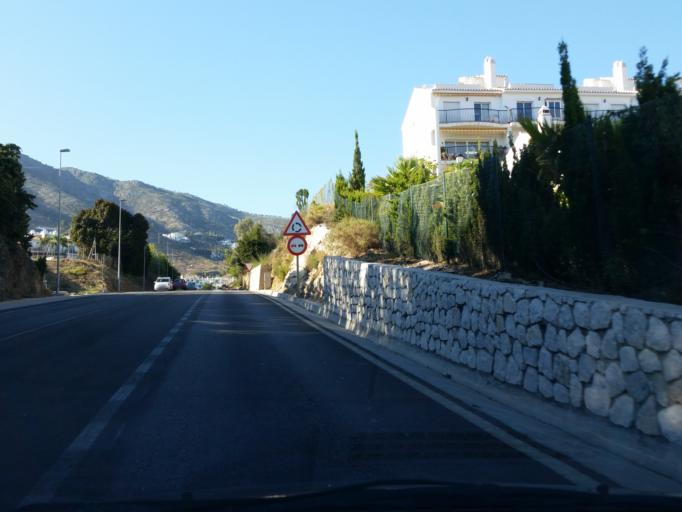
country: ES
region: Andalusia
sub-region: Provincia de Malaga
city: Mijas
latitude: 36.5793
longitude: -4.6364
